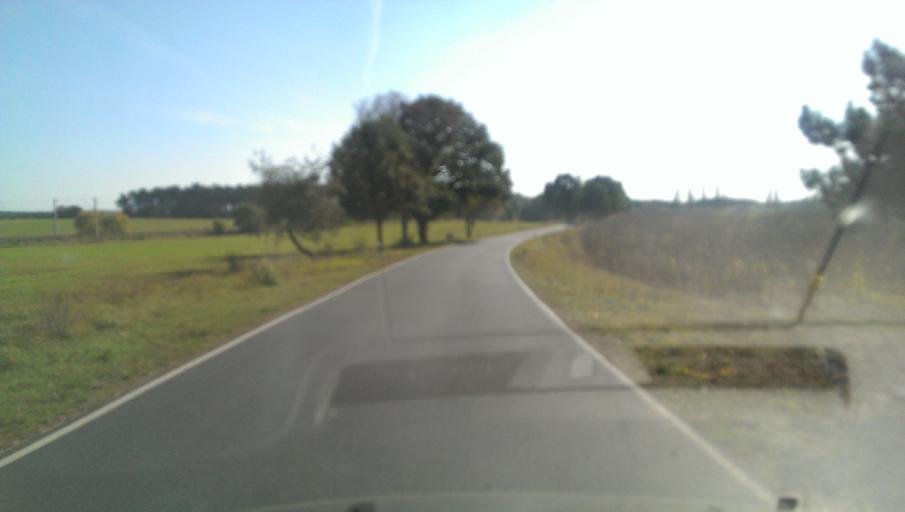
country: DE
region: Brandenburg
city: Halbe
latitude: 52.0627
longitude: 13.7226
